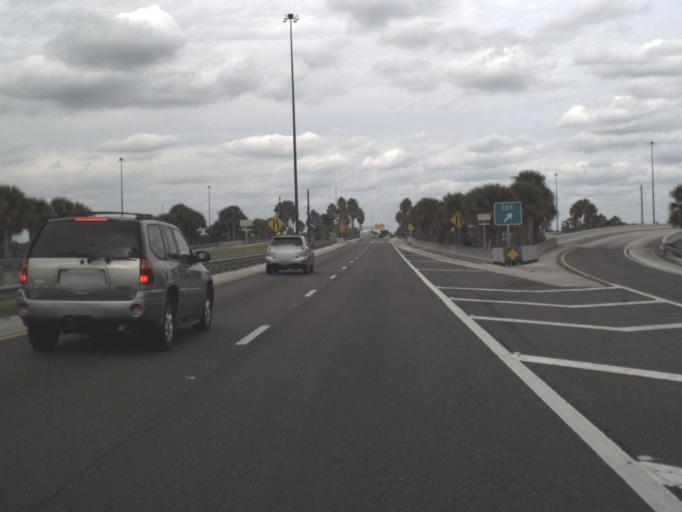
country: US
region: Florida
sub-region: Polk County
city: Winston
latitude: 28.0333
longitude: -82.0400
